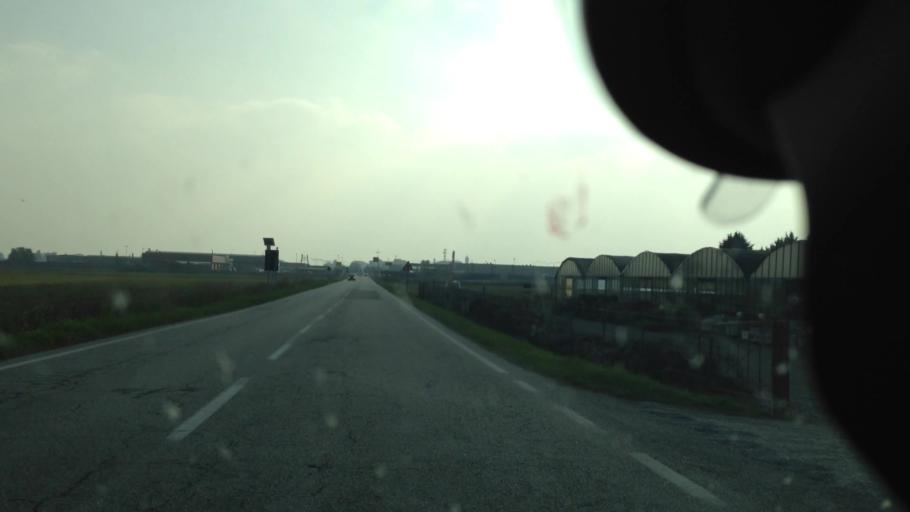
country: IT
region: Piedmont
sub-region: Provincia di Vercelli
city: Cigliano
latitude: 45.3233
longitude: 8.0338
